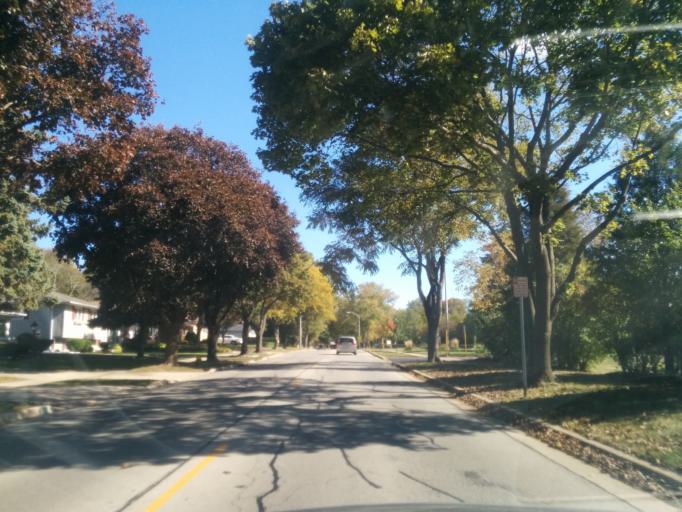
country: US
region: Illinois
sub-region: DuPage County
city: Lombard
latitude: 41.8745
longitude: -88.0260
